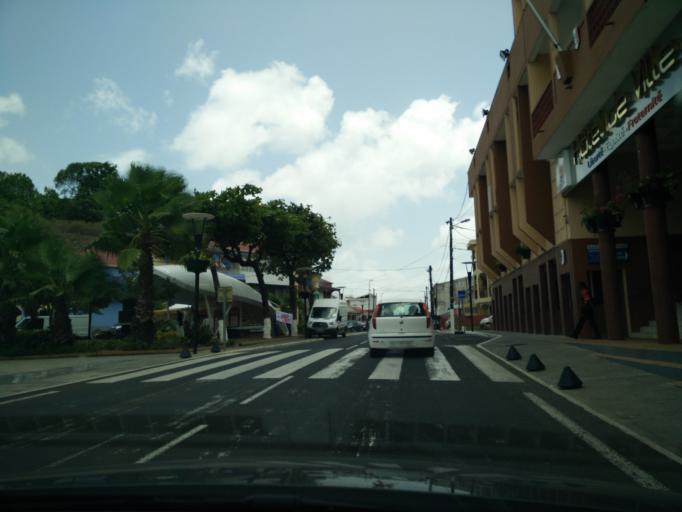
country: GP
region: Guadeloupe
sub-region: Guadeloupe
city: Les Abymes
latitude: 16.2712
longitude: -61.5051
